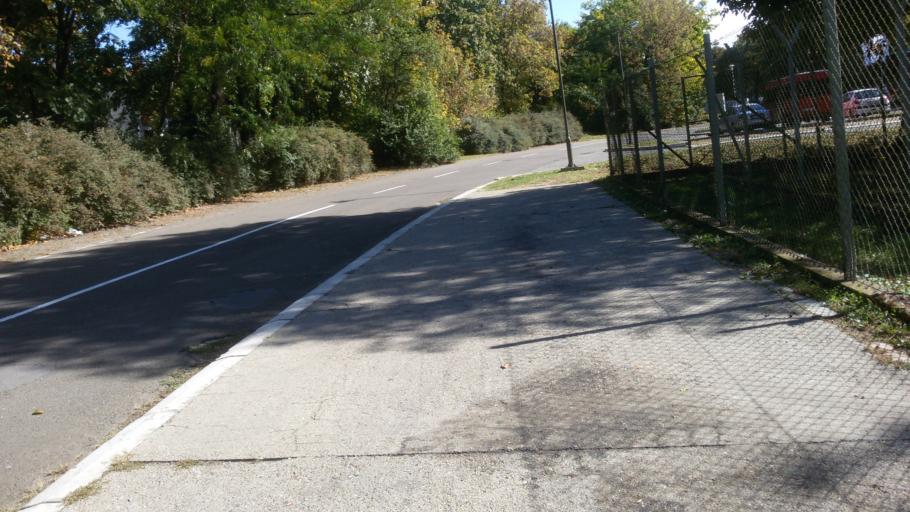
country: RS
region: Central Serbia
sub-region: Belgrade
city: Rakovica
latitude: 44.7480
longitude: 20.4037
